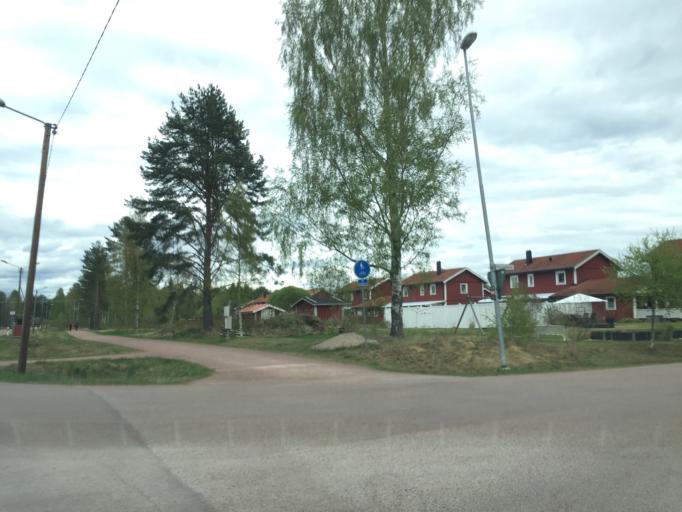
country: SE
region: Dalarna
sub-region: Mora Kommun
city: Mora
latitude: 61.0280
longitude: 14.5126
